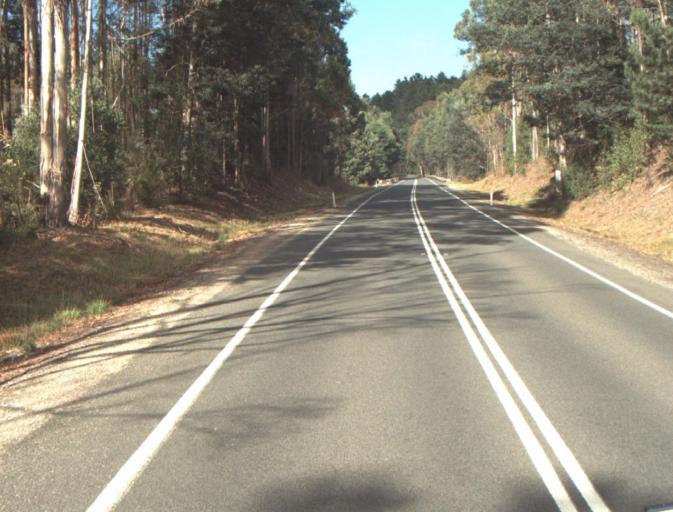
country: AU
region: Tasmania
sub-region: Launceston
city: Mayfield
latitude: -41.2982
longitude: 147.2107
